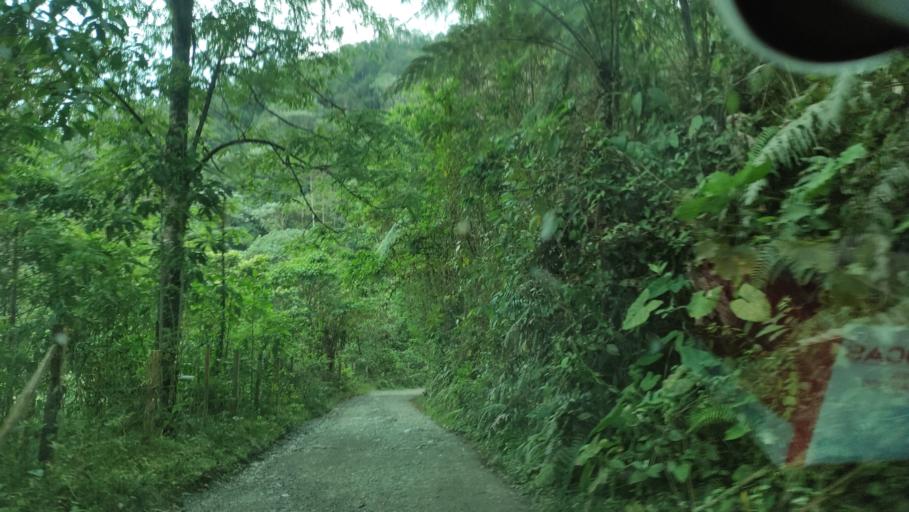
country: CO
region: Valle del Cauca
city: San Pedro
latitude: 3.8809
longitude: -76.1504
